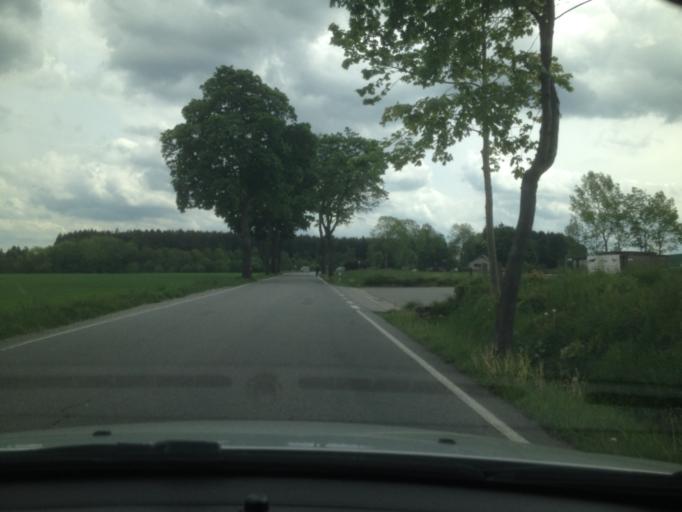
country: DE
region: Saxony
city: Zwonitz
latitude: 50.6494
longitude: 12.7785
